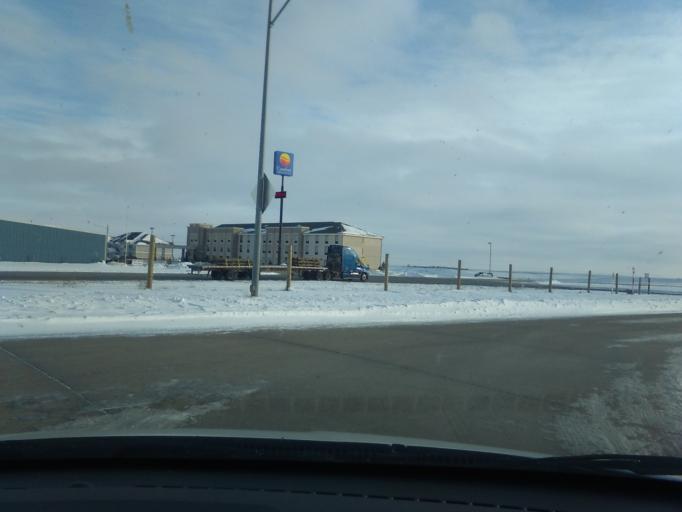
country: US
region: Nebraska
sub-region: Cheyenne County
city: Sidney
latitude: 41.1109
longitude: -102.9499
